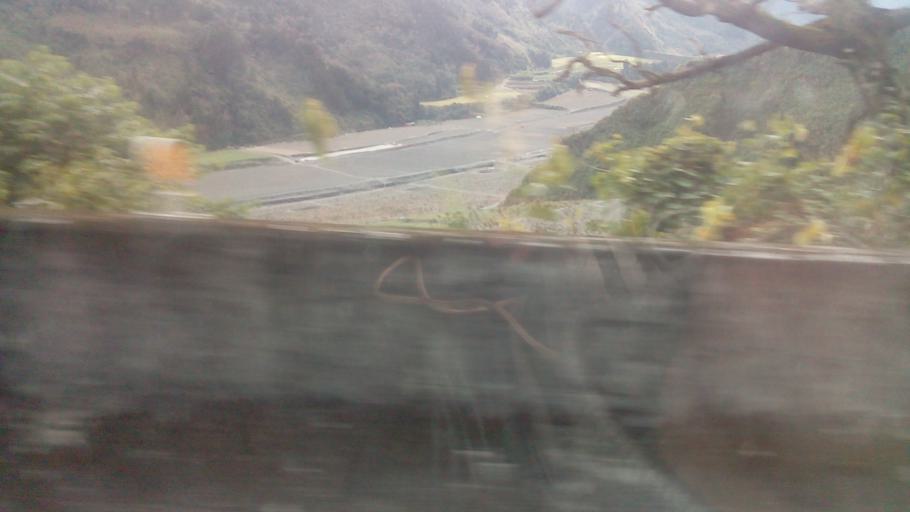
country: TW
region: Taiwan
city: Daxi
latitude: 24.4629
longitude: 121.3968
